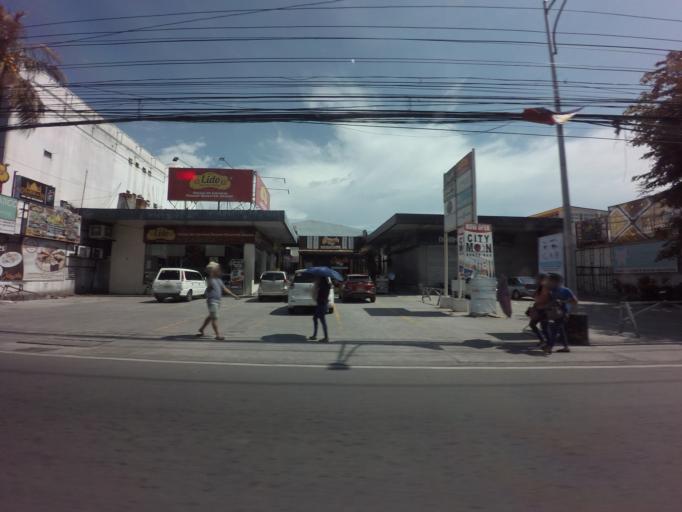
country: PH
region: Calabarzon
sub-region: Province of Rizal
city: Las Pinas
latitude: 14.4483
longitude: 120.9843
